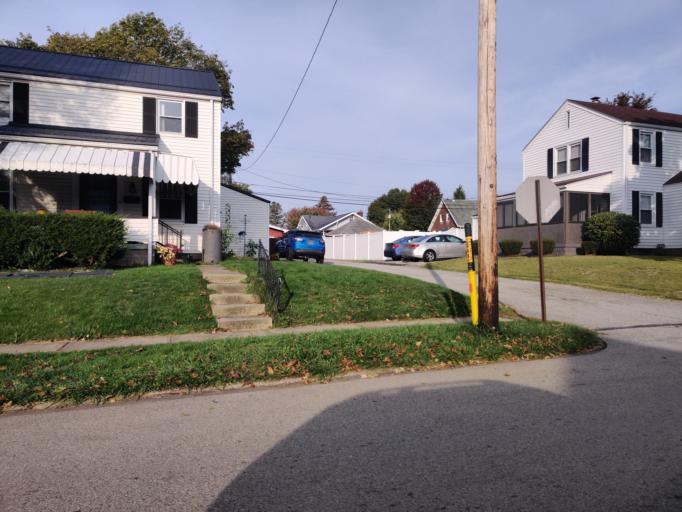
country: US
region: Pennsylvania
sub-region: Allegheny County
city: Brackenridge
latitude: 40.6277
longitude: -79.7254
